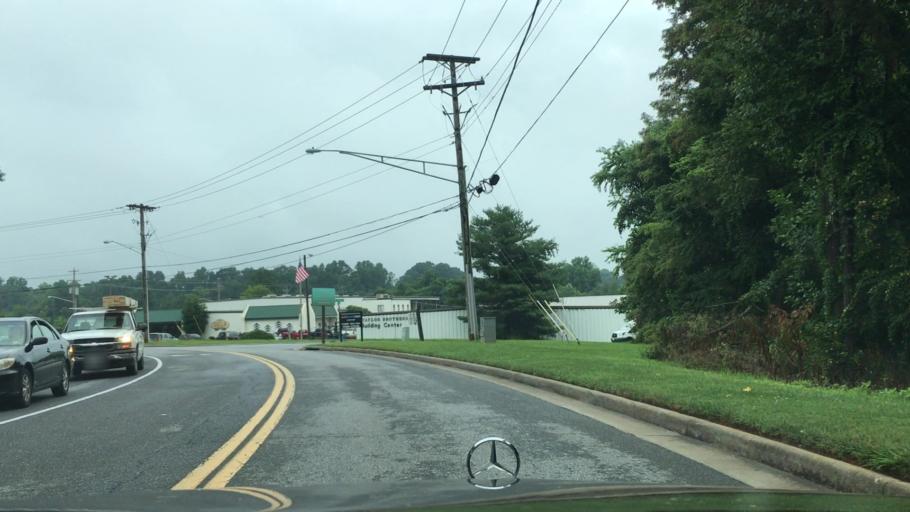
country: US
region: Virginia
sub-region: City of Lynchburg
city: West Lynchburg
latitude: 37.3744
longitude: -79.2246
